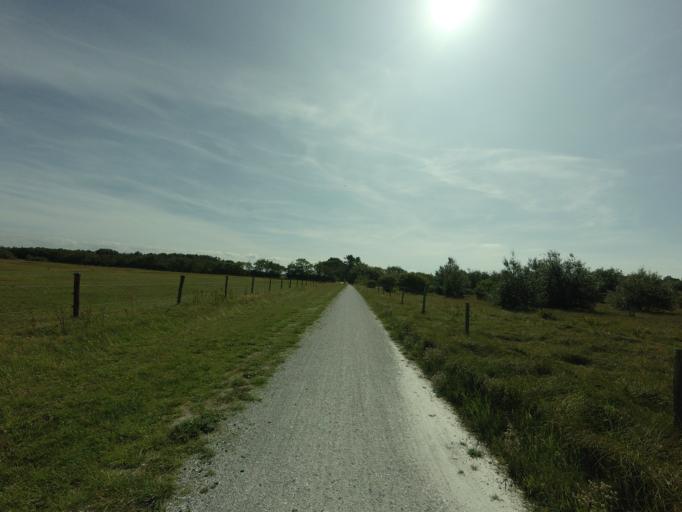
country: NL
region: Friesland
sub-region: Gemeente Ameland
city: Hollum
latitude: 53.4465
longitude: 5.6554
